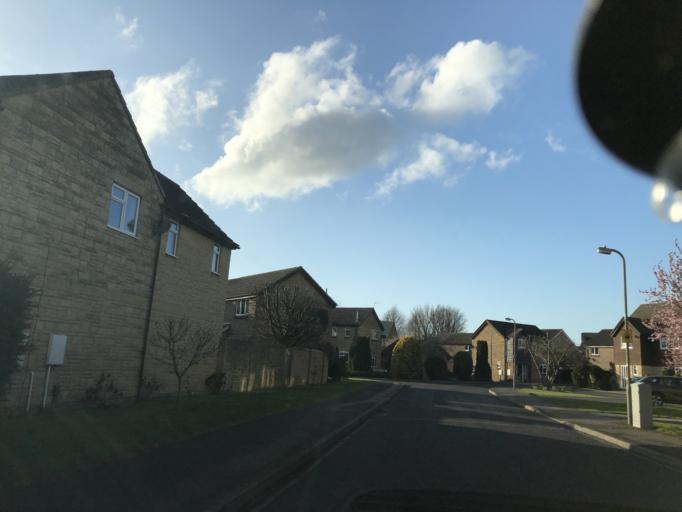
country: GB
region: England
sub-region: Oxfordshire
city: Witney
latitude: 51.7766
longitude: -1.4996
